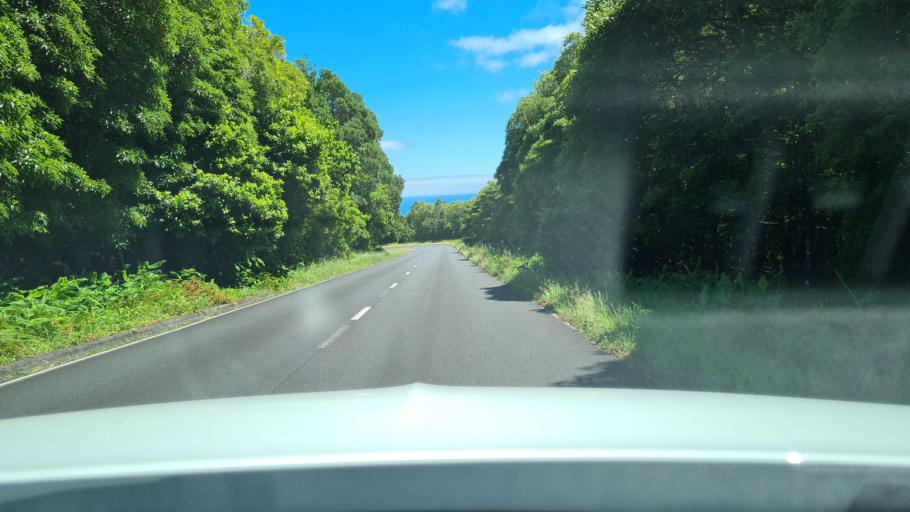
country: PT
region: Azores
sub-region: Sao Roque do Pico
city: Sao Roque do Pico
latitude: 38.4278
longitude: -28.2912
